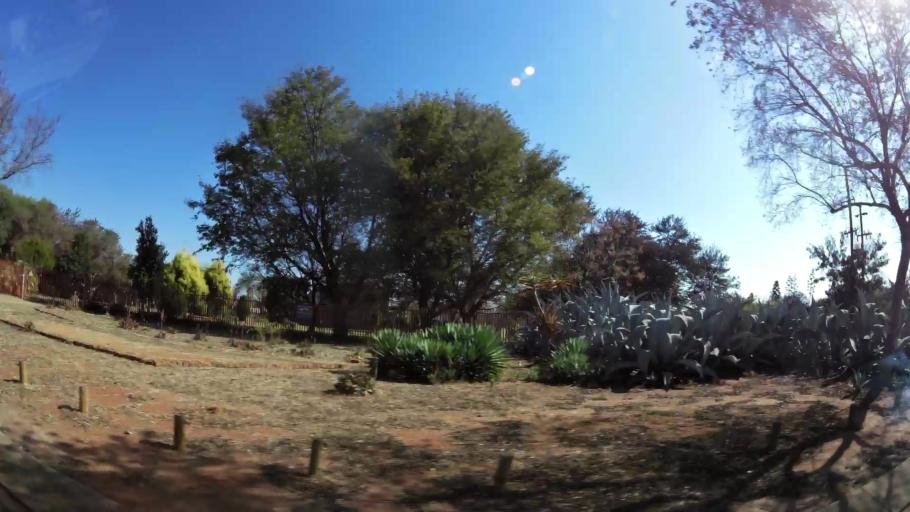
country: ZA
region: Gauteng
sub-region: City of Tshwane Metropolitan Municipality
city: Pretoria
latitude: -25.6521
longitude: 28.2630
